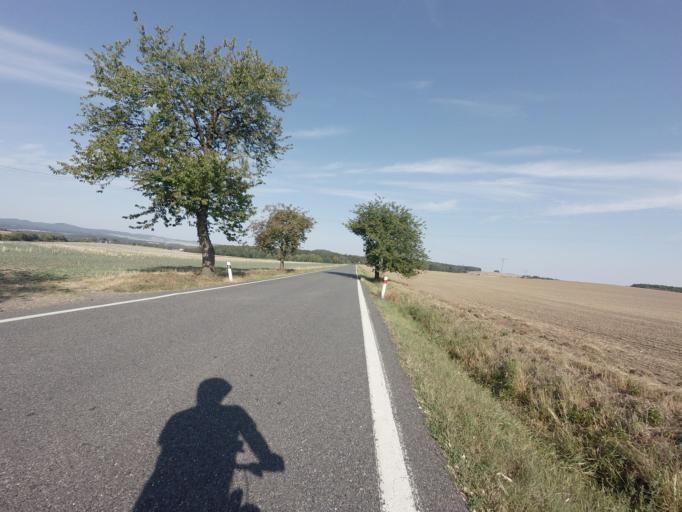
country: CZ
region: Jihocesky
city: Bernartice
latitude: 49.3086
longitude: 14.3777
